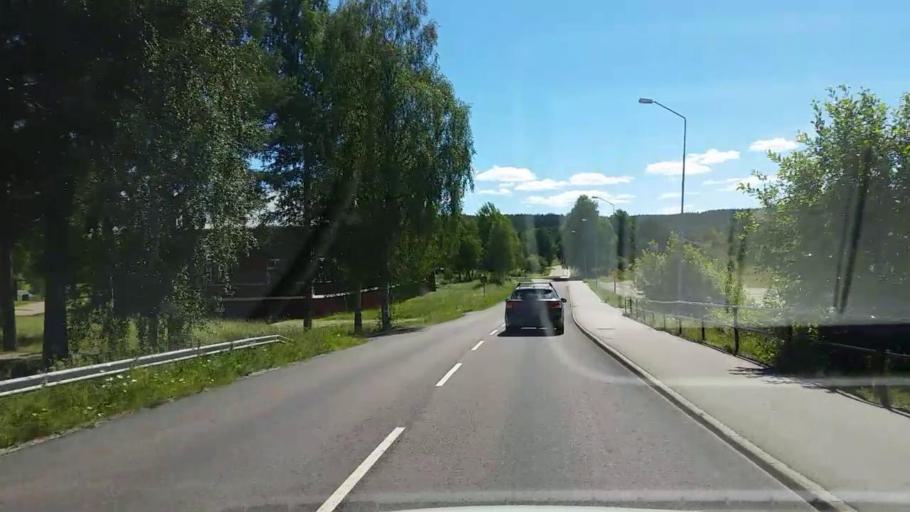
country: SE
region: Gaevleborg
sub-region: Ovanakers Kommun
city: Edsbyn
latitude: 61.3713
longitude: 15.8176
